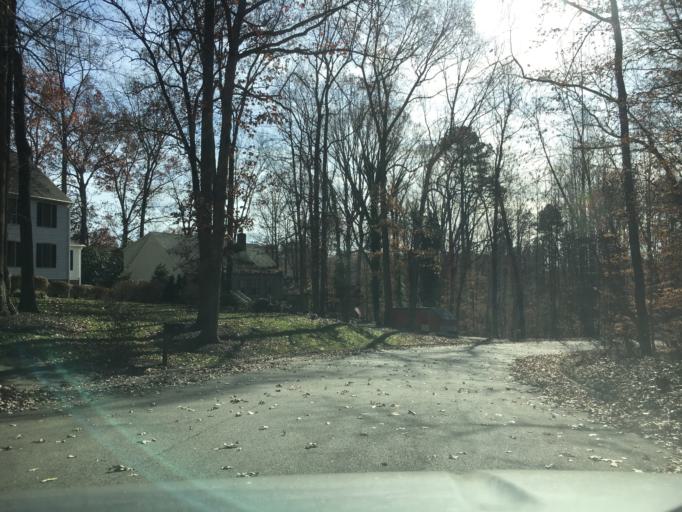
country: US
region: Virginia
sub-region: Halifax County
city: South Boston
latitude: 36.7086
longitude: -78.9165
